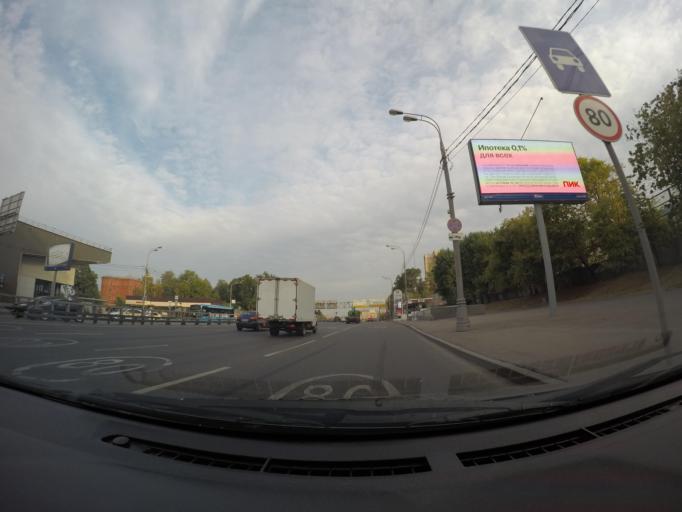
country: RU
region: Moscow
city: Sokol'niki
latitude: 55.7847
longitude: 37.6642
